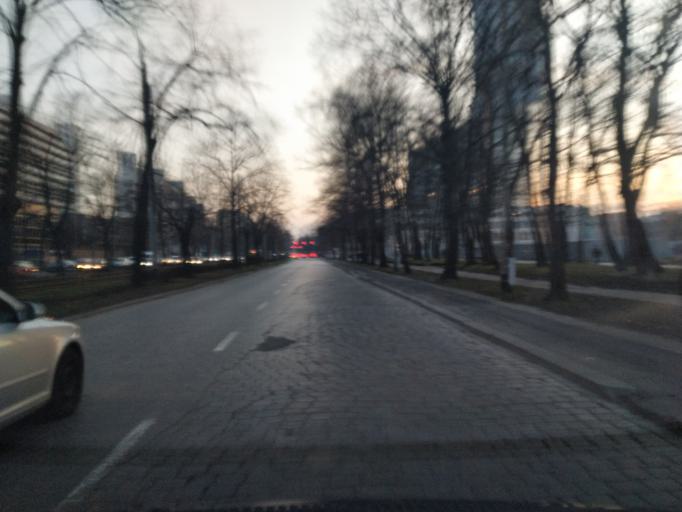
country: PL
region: Lower Silesian Voivodeship
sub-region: Powiat wroclawski
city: Wroclaw
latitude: 51.0966
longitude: 17.0238
